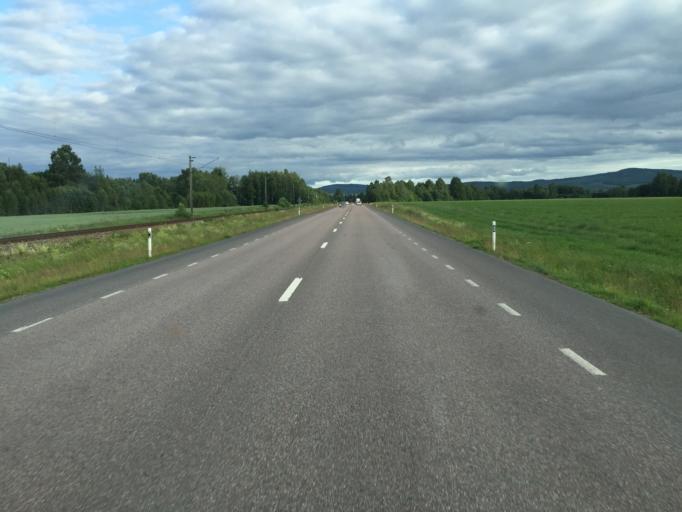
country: SE
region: Dalarna
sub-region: Gagnefs Kommun
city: Djuras
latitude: 60.5733
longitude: 15.1239
